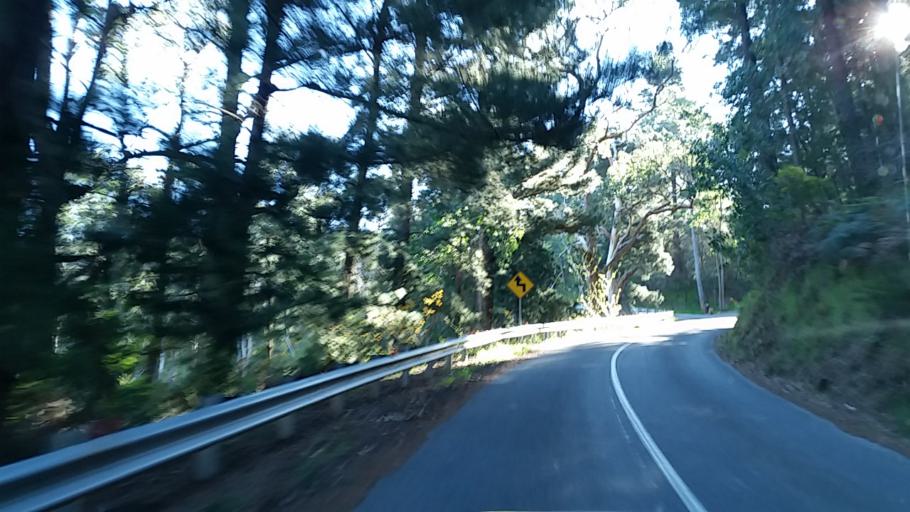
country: AU
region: South Australia
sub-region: Adelaide Hills
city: Adelaide Hills
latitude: -34.9308
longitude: 138.7617
